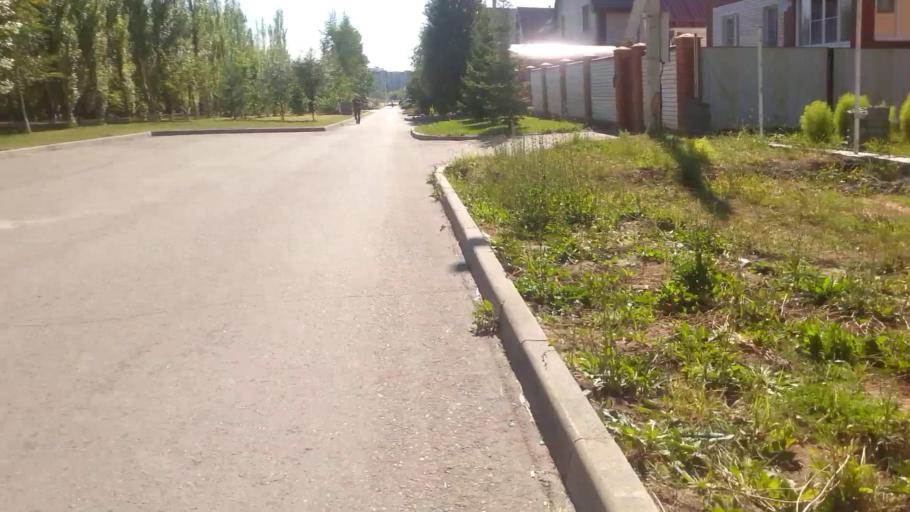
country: RU
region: Altai Krai
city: Novosilikatnyy
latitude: 53.3534
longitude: 83.6549
